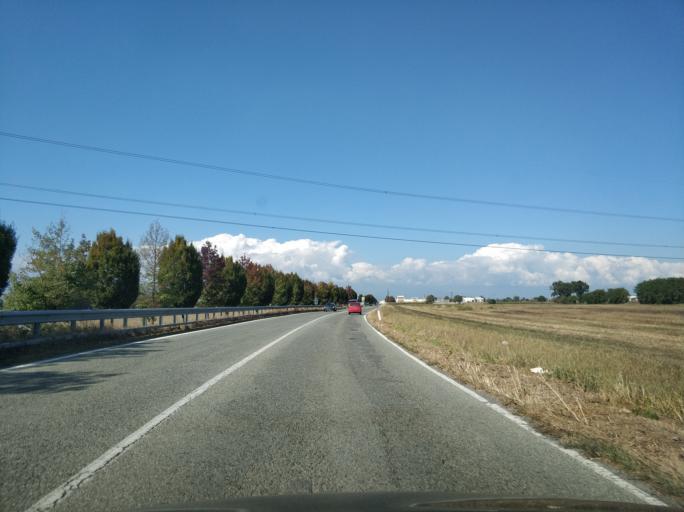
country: IT
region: Piedmont
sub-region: Provincia di Torino
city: Borgaro Torinese
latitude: 45.1433
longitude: 7.6795
